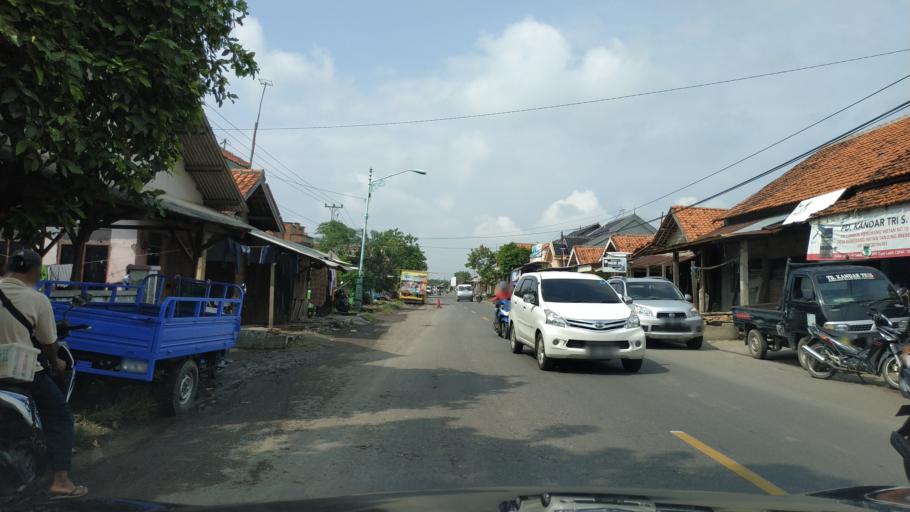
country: ID
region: Central Java
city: Ketanggungan
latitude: -6.8814
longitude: 108.8854
